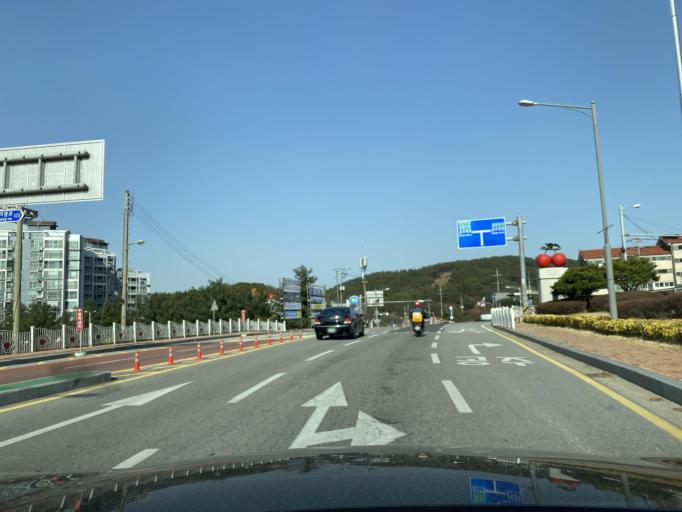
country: KR
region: Chungcheongnam-do
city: Yesan
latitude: 36.6870
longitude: 126.8430
